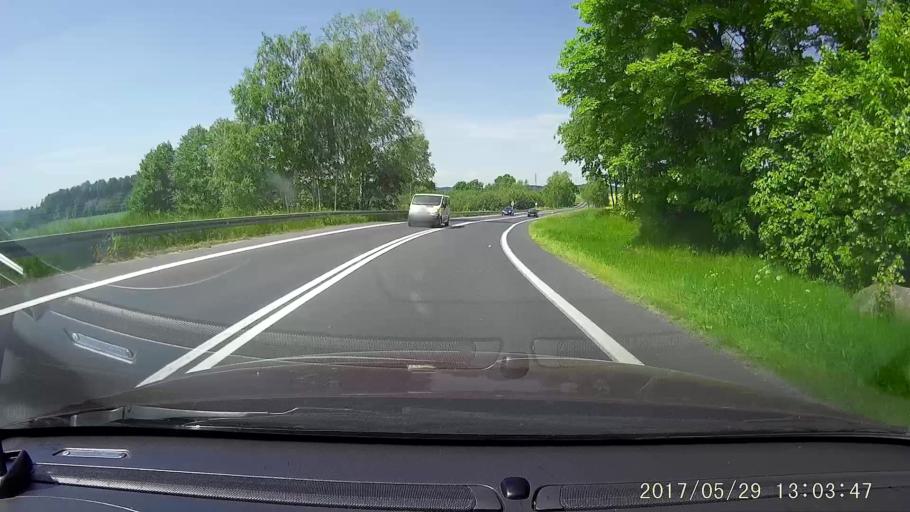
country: PL
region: Lower Silesian Voivodeship
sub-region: Powiat jeleniogorski
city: Stara Kamienica
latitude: 50.9253
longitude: 15.6080
